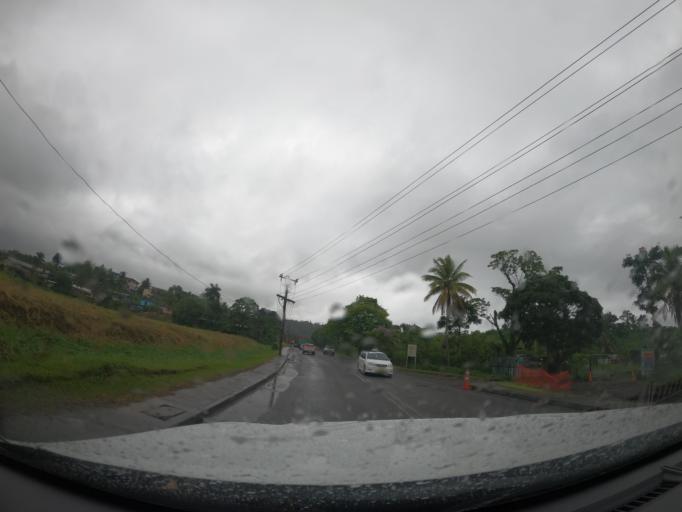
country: FJ
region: Central
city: Suva
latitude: -18.1136
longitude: 178.4273
